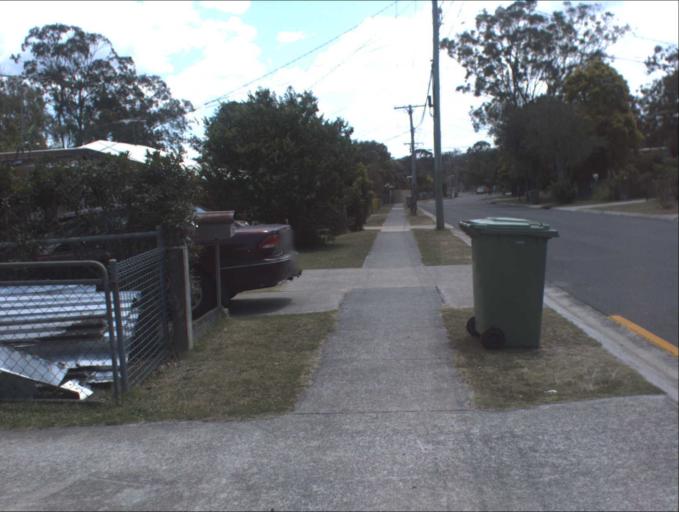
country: AU
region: Queensland
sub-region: Logan
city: Logan City
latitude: -27.6534
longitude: 153.1016
